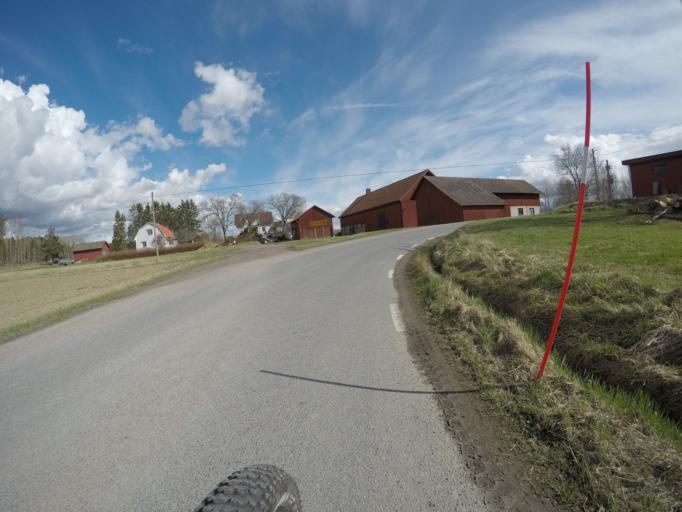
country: SE
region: Vaestmanland
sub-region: Kungsors Kommun
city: Kungsoer
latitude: 59.3023
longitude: 16.1383
